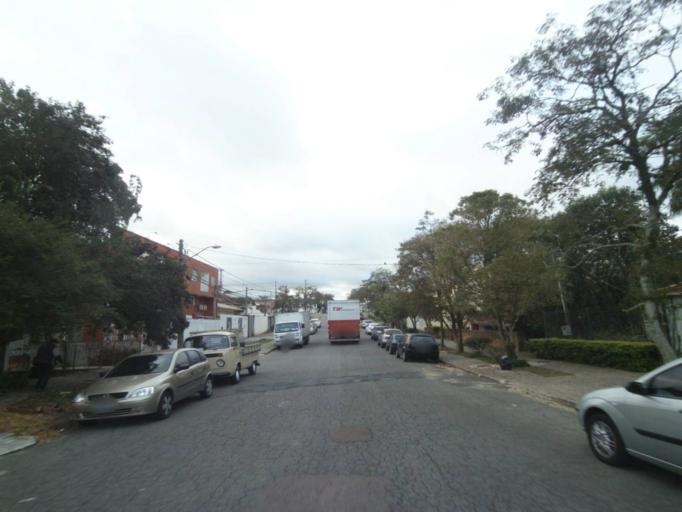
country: BR
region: Parana
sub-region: Curitiba
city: Curitiba
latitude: -25.4562
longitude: -49.2607
